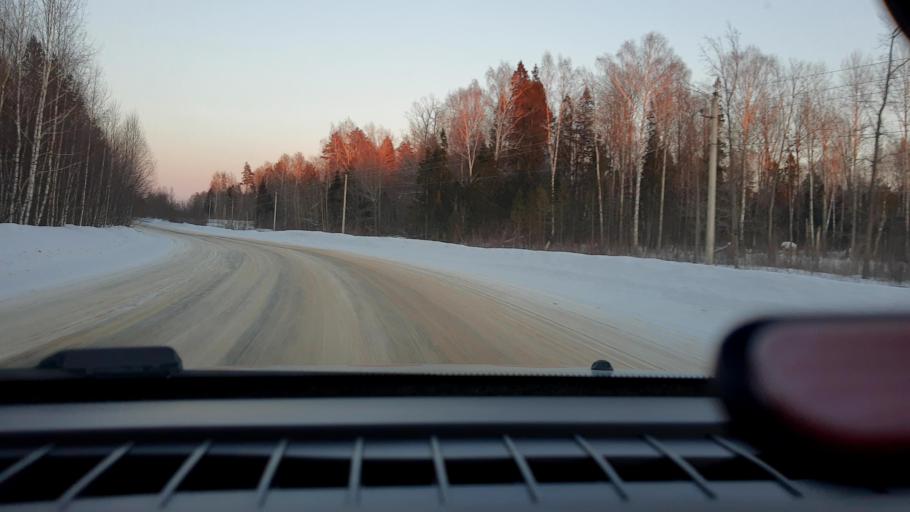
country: RU
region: Nizjnij Novgorod
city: Lyskovo
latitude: 56.1609
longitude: 45.2056
